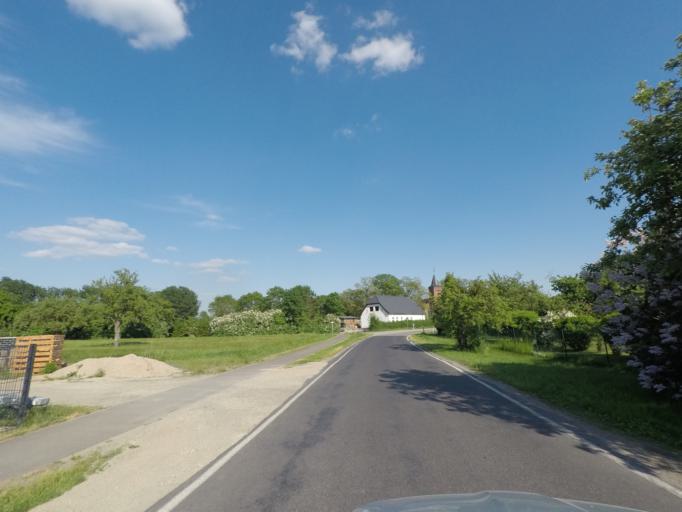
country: DE
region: Brandenburg
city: Hohenfinow
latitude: 52.7307
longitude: 13.8691
